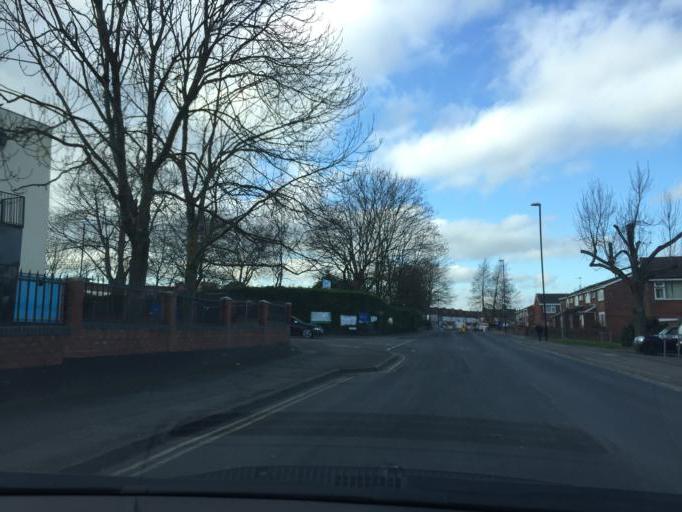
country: GB
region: England
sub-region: Coventry
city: Coventry
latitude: 52.4139
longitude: -1.4989
